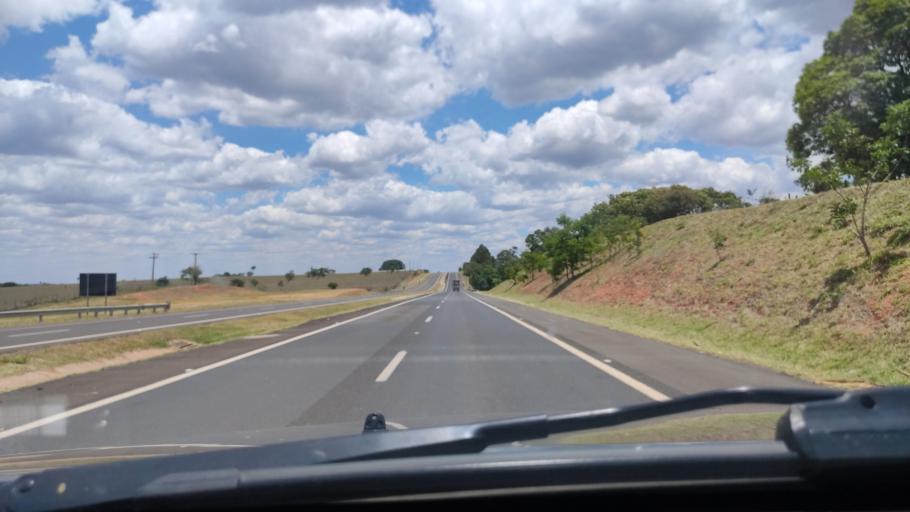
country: BR
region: Sao Paulo
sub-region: Duartina
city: Duartina
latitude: -22.4981
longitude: -49.2692
